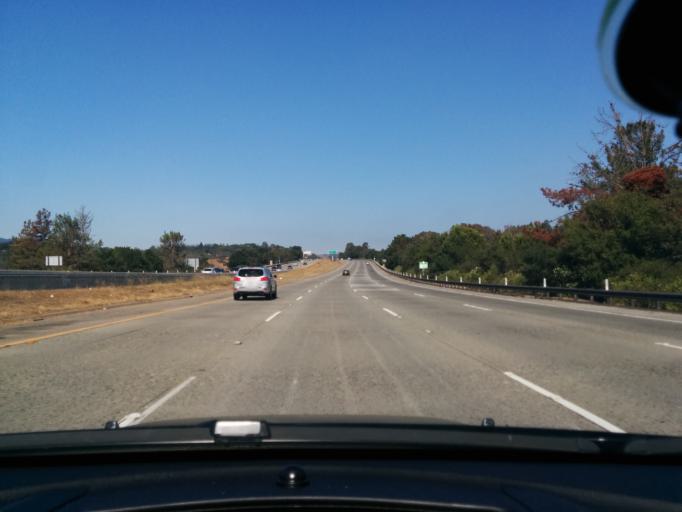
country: US
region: California
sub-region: San Mateo County
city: Woodside
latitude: 37.4247
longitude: -122.2293
